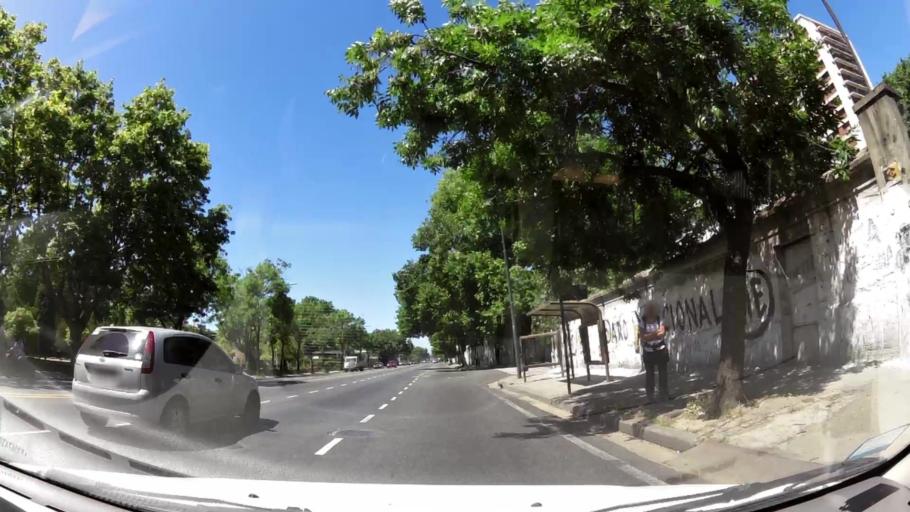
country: AR
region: Buenos Aires F.D.
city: Buenos Aires
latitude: -34.6131
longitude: -58.3670
